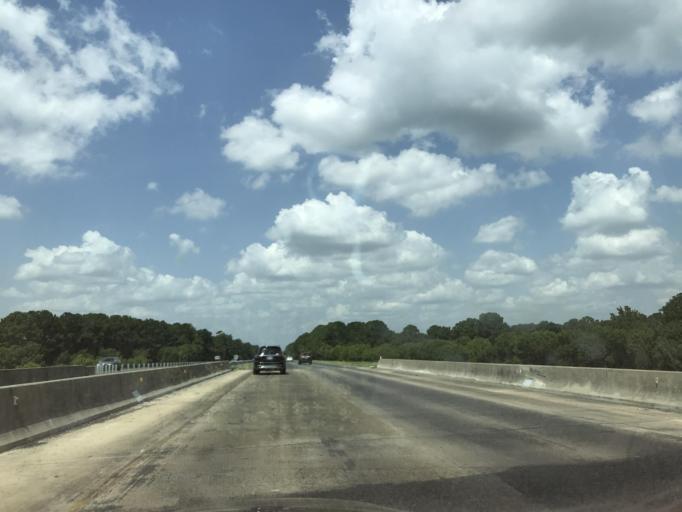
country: US
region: North Carolina
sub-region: Duplin County
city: Wallace
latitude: 34.7549
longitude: -77.9503
